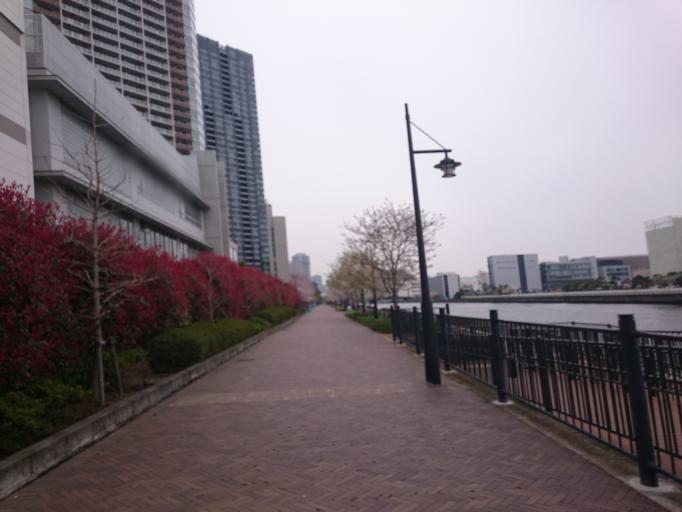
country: JP
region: Tokyo
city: Urayasu
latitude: 35.6583
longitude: 139.7989
